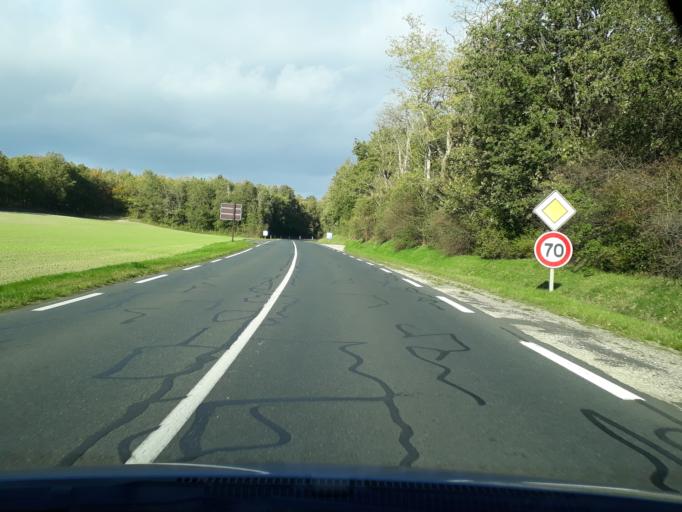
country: FR
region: Centre
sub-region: Departement du Loiret
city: Malesherbes
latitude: 48.3033
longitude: 2.4359
